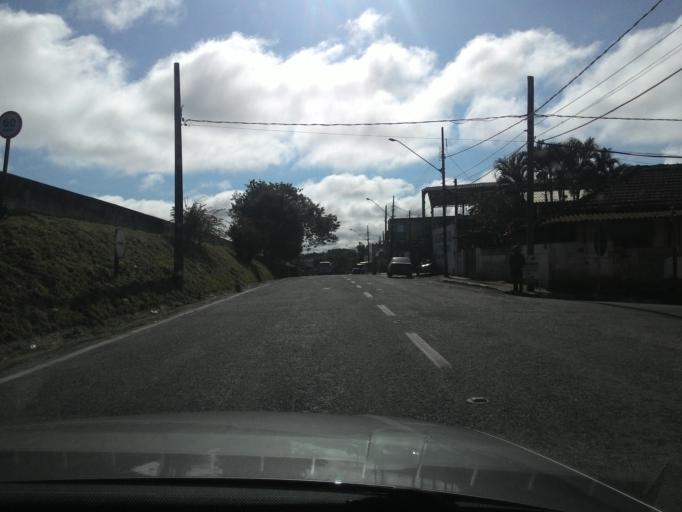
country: BR
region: Sao Paulo
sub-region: Registro
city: Registro
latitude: -24.4922
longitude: -47.8364
